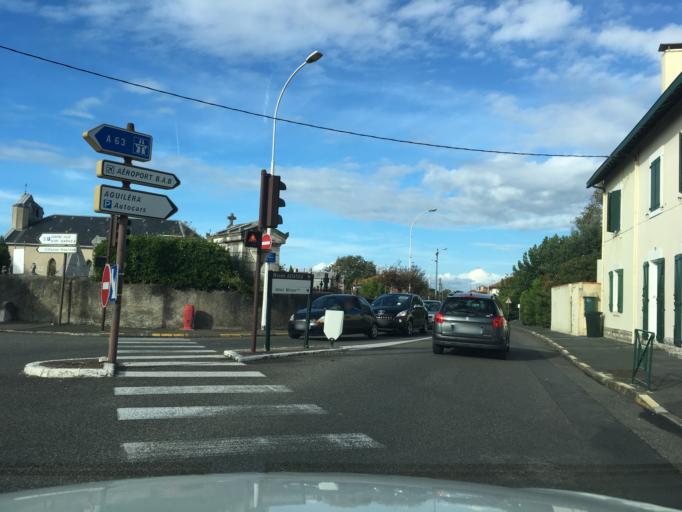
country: FR
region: Aquitaine
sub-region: Departement des Pyrenees-Atlantiques
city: Biarritz
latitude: 43.4730
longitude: -1.5558
